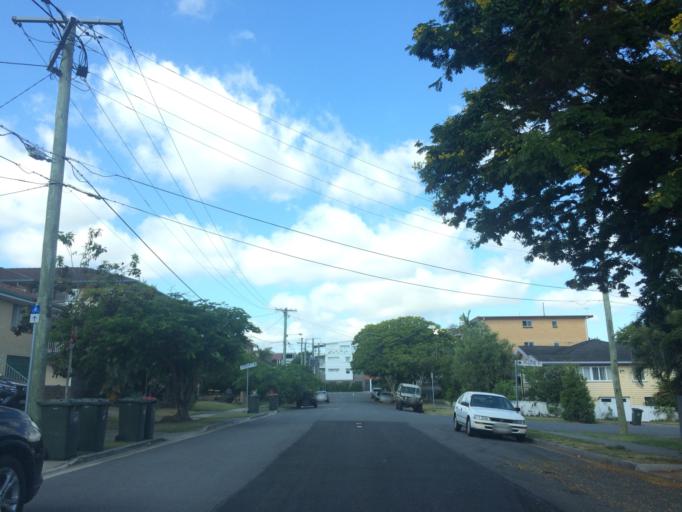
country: AU
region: Queensland
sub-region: Brisbane
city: Seven Hills
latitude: -27.4905
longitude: 153.0607
